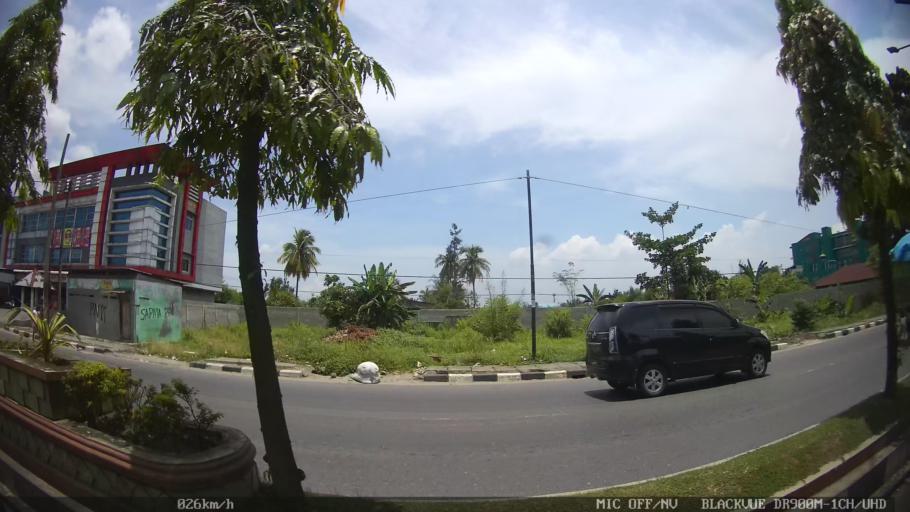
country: ID
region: North Sumatra
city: Binjai
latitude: 3.6067
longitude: 98.5258
